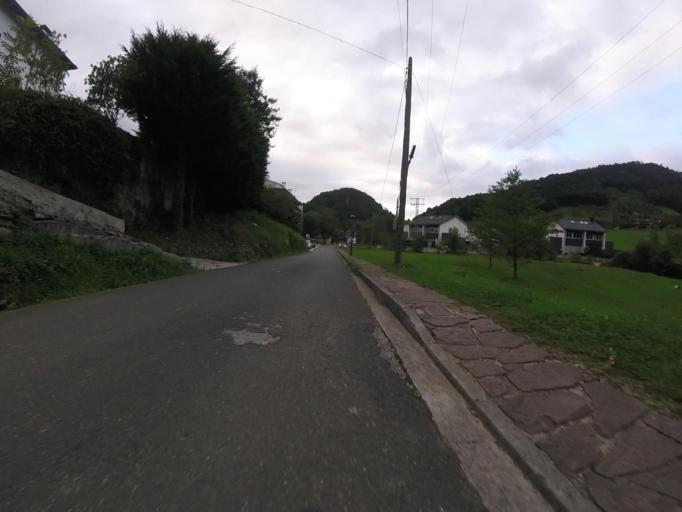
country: ES
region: Basque Country
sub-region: Provincia de Guipuzcoa
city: Errenteria
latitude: 43.2819
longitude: -1.8516
